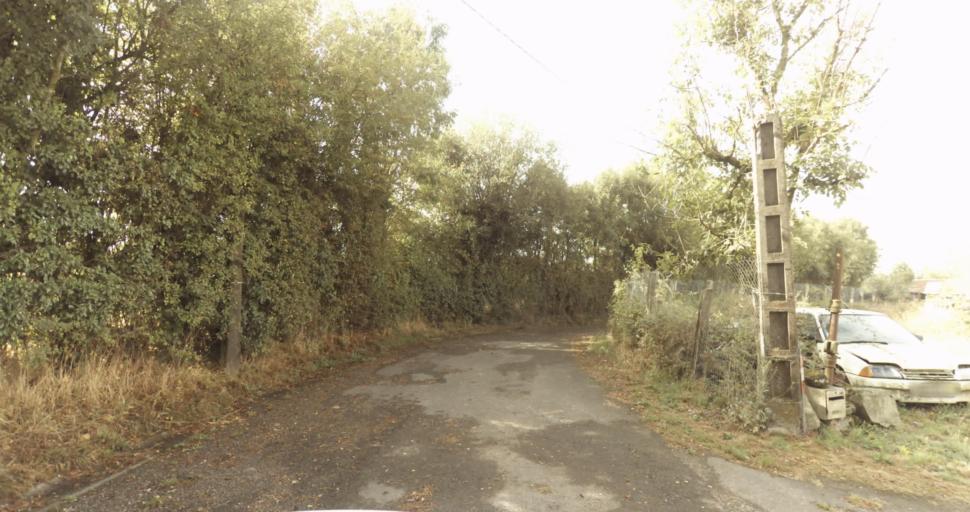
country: FR
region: Lower Normandy
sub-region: Departement de l'Orne
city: Gace
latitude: 48.8494
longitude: 0.3641
